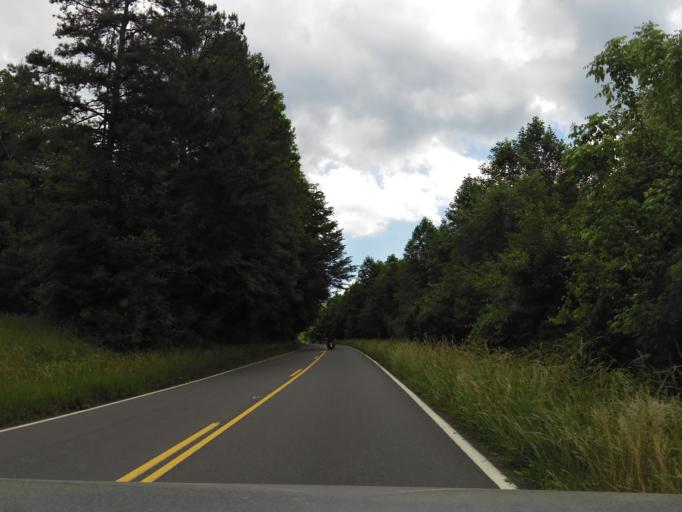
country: US
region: Tennessee
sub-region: Loudon County
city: Greenback
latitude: 35.5467
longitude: -84.0620
